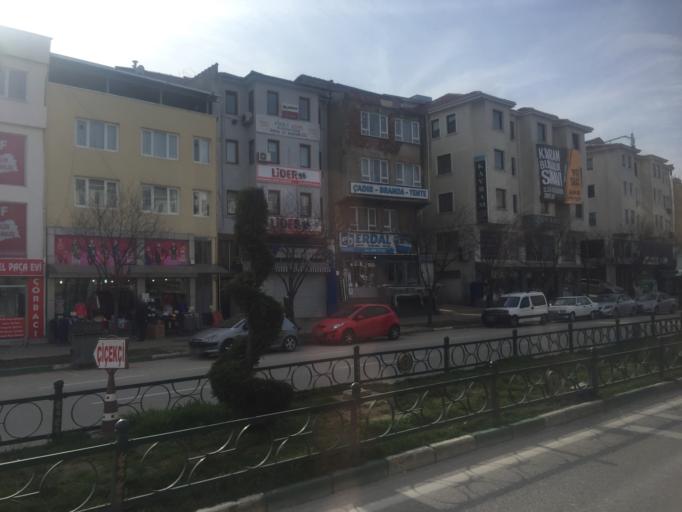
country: TR
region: Bursa
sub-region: Osmangazi
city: Bursa
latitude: 40.1876
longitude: 29.0674
